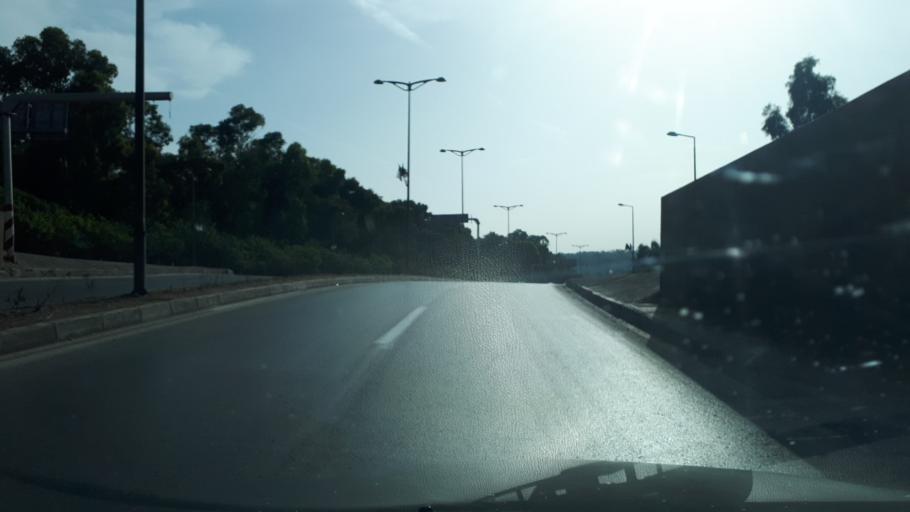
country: DZ
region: Alger
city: Algiers
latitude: 36.7650
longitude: 3.0074
